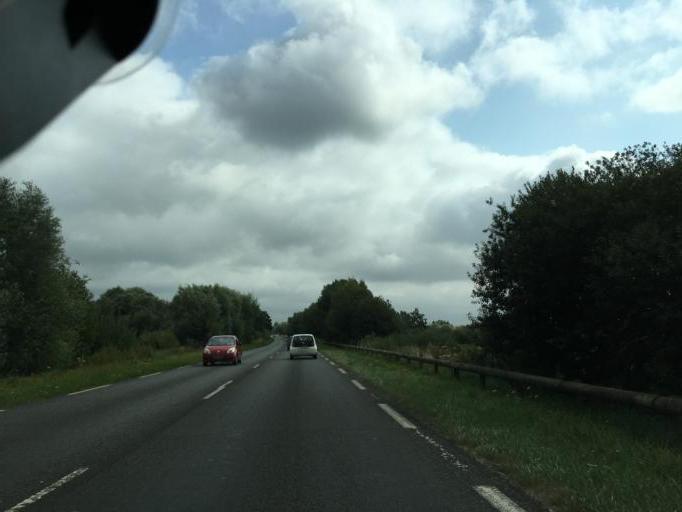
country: FR
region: Nord-Pas-de-Calais
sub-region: Departement du Pas-de-Calais
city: Rang-du-Fliers
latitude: 50.4064
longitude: 1.6244
